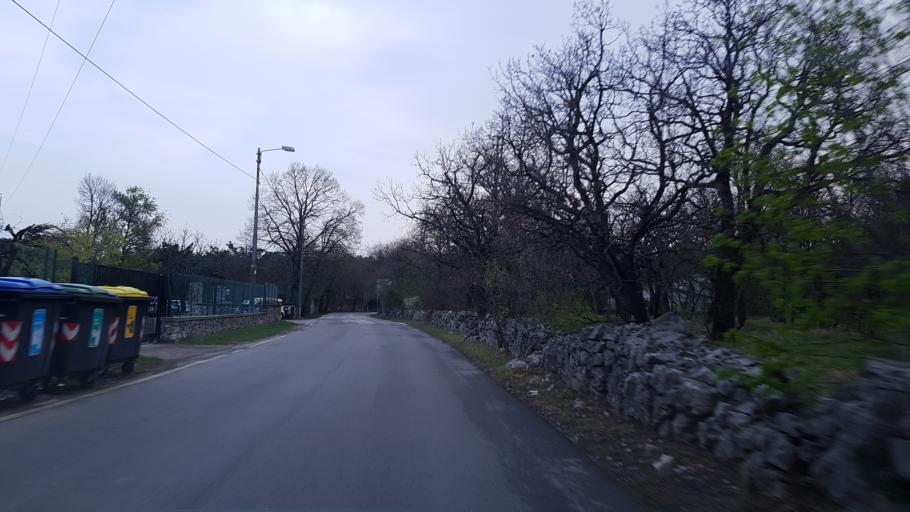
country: IT
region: Friuli Venezia Giulia
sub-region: Provincia di Trieste
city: Domio
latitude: 45.6512
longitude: 13.8391
